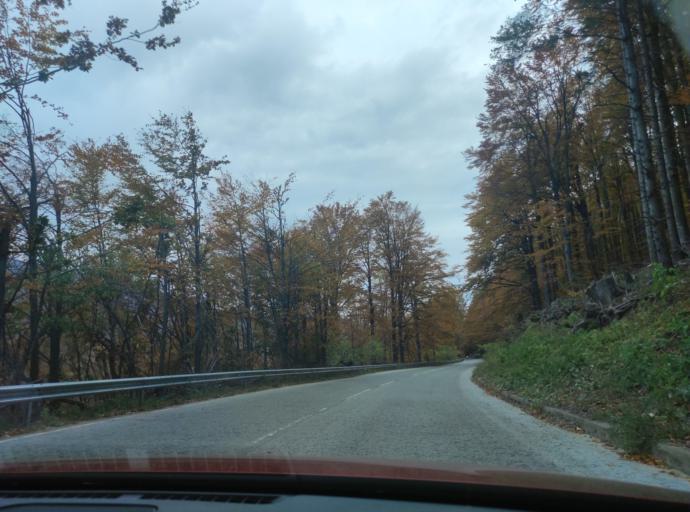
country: BG
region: Montana
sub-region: Obshtina Berkovitsa
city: Berkovitsa
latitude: 43.1407
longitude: 23.1423
